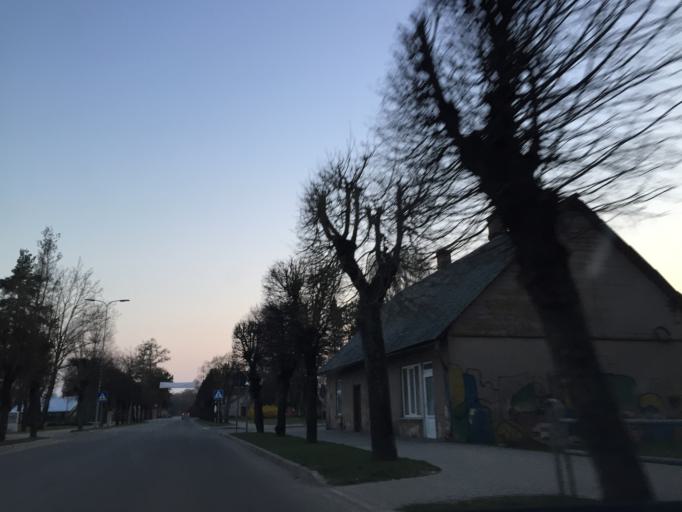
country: LV
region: Valkas Rajons
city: Valka
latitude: 57.7737
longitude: 26.0189
